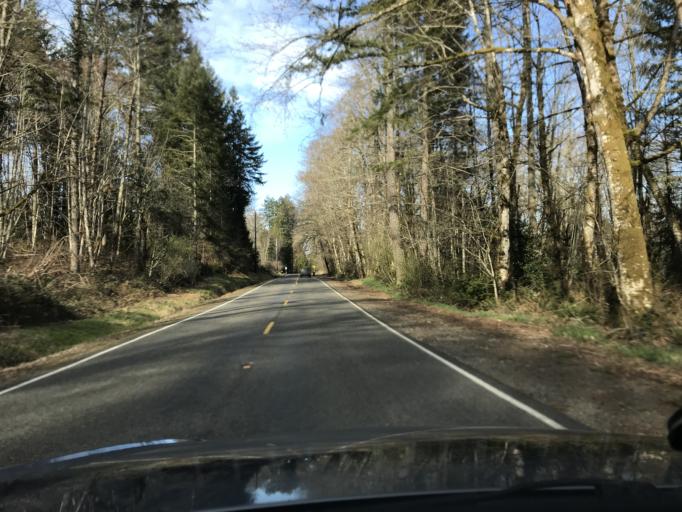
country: US
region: Washington
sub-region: Pierce County
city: Home
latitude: 47.2399
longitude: -122.7866
